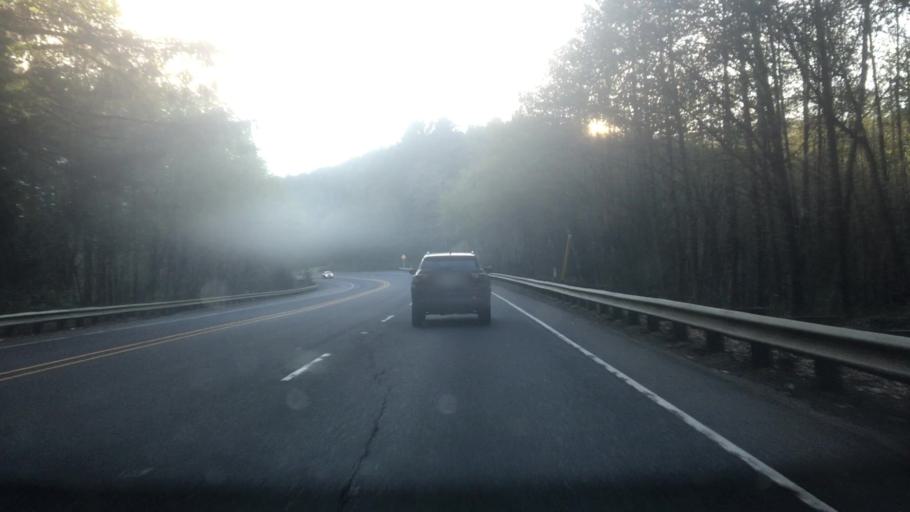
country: US
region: Oregon
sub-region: Clatsop County
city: Cannon Beach
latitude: 45.9214
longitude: -123.9356
